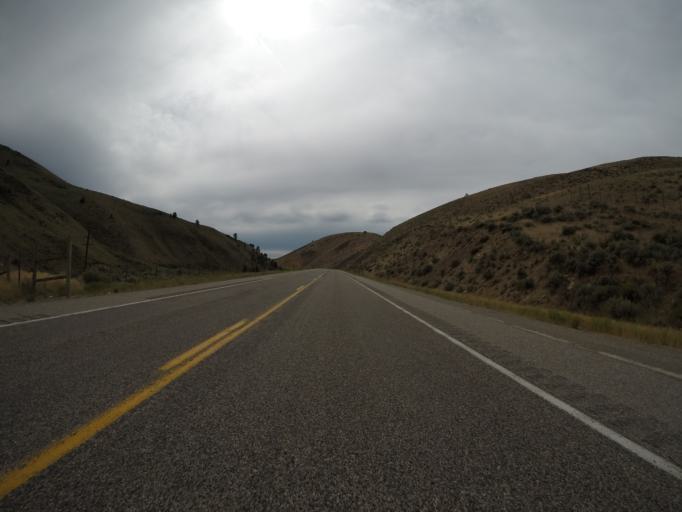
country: US
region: Wyoming
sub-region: Lincoln County
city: Kemmerer
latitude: 41.8250
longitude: -110.8440
